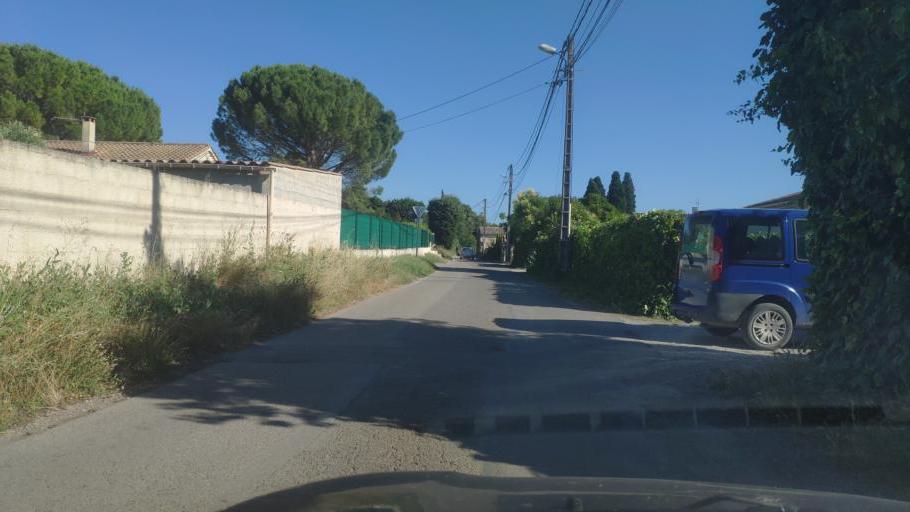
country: FR
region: Provence-Alpes-Cote d'Azur
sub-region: Departement du Vaucluse
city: Carpentras
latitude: 44.0727
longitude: 5.0490
